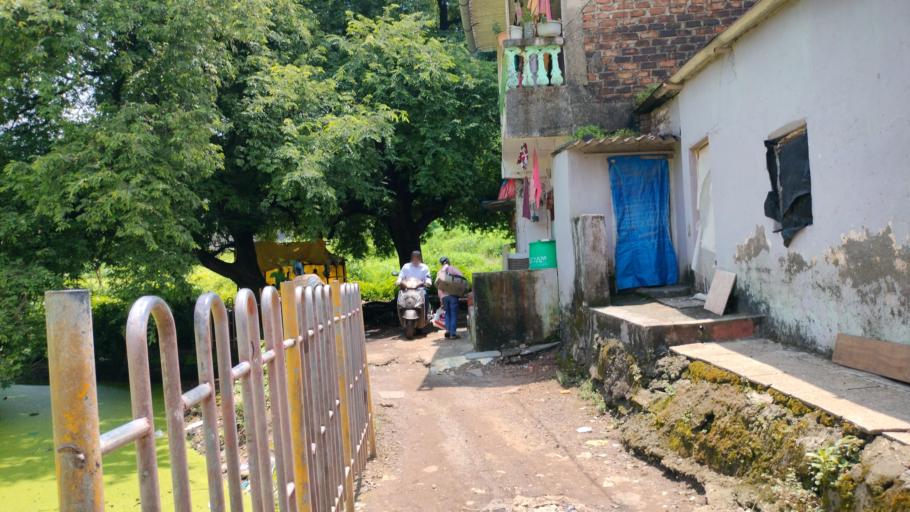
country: IN
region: Maharashtra
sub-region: Thane
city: Virar
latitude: 19.4787
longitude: 72.8203
